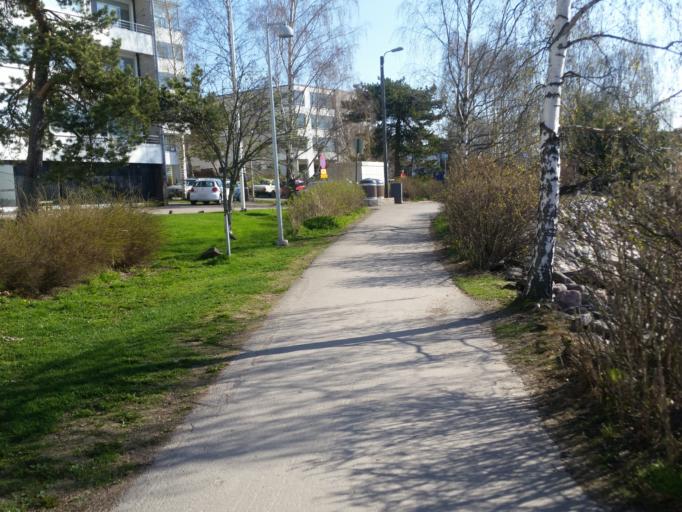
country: FI
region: Uusimaa
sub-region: Helsinki
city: Helsinki
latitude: 60.1583
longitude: 24.8916
